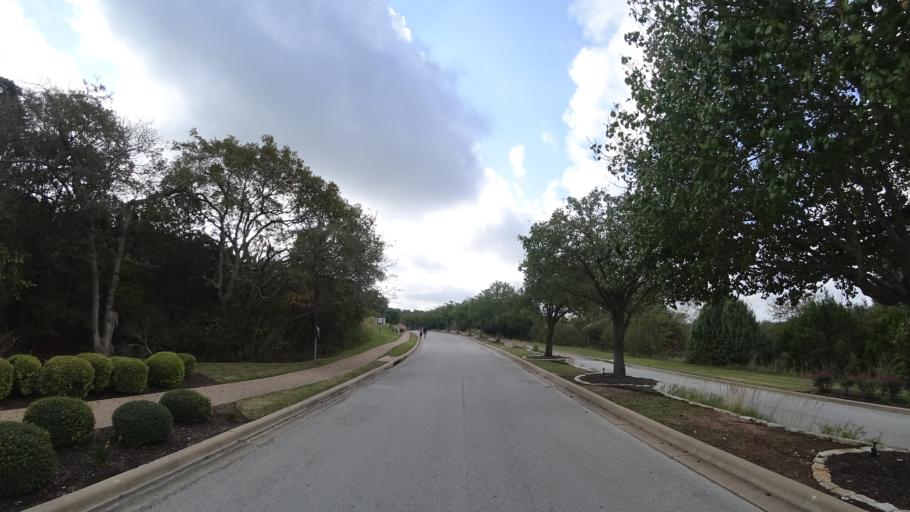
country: US
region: Texas
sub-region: Travis County
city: Barton Creek
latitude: 30.3086
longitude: -97.8972
